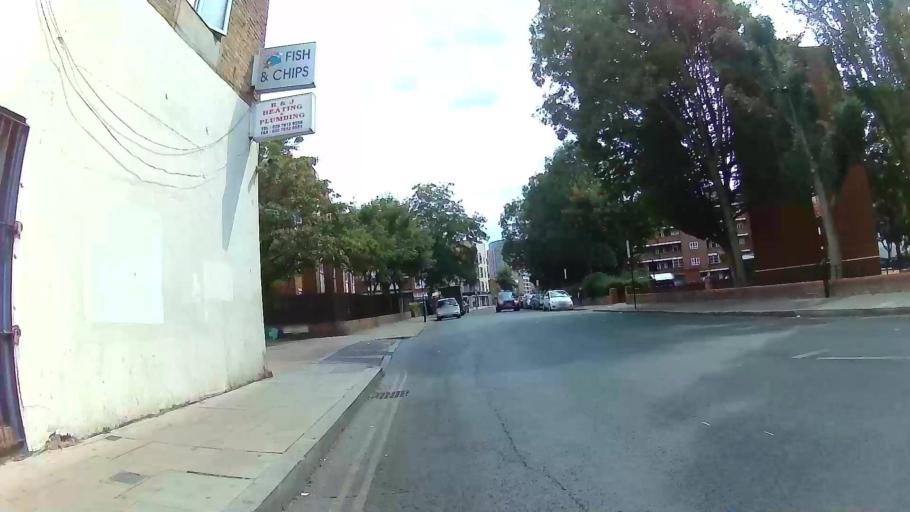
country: GB
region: England
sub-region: Greater London
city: Islington
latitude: 51.5515
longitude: -0.0792
